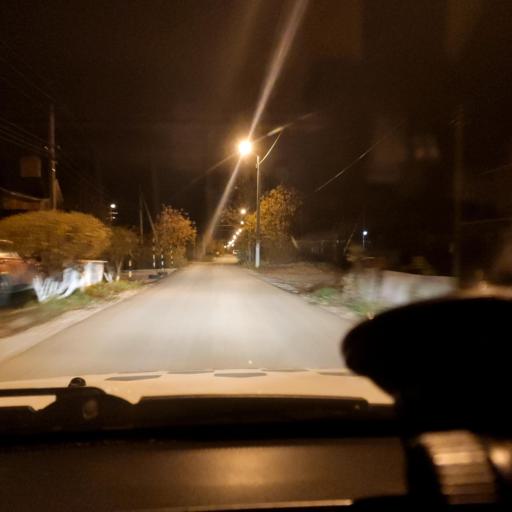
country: RU
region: Perm
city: Perm
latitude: 57.9790
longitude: 56.3097
